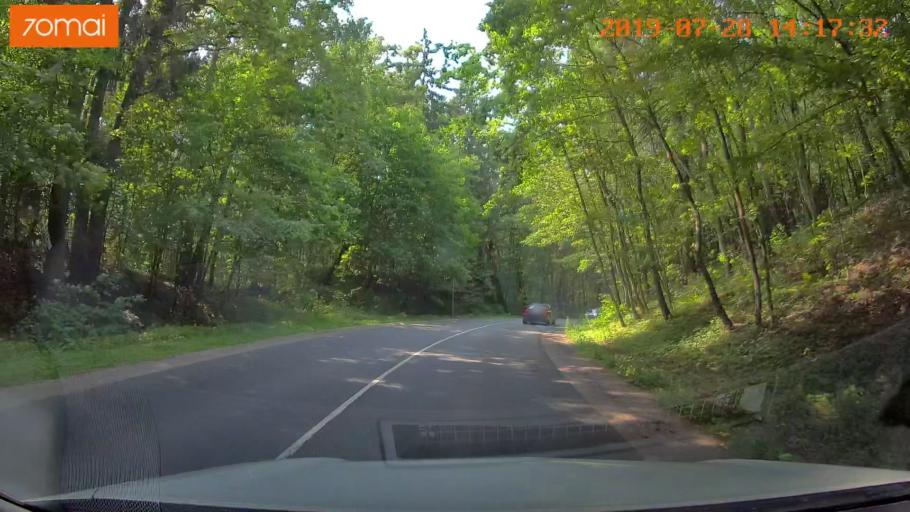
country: RU
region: Kaliningrad
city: Volochayevskoye
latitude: 54.8152
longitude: 20.2531
